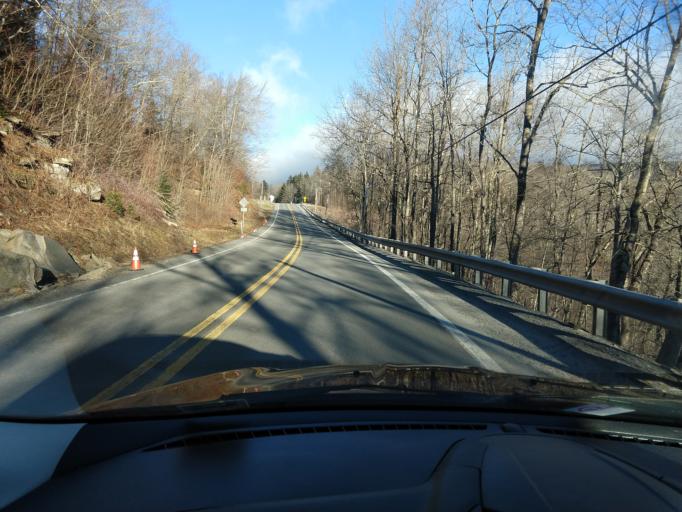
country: US
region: Virginia
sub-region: Highland County
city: Monterey
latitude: 38.5969
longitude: -79.8478
